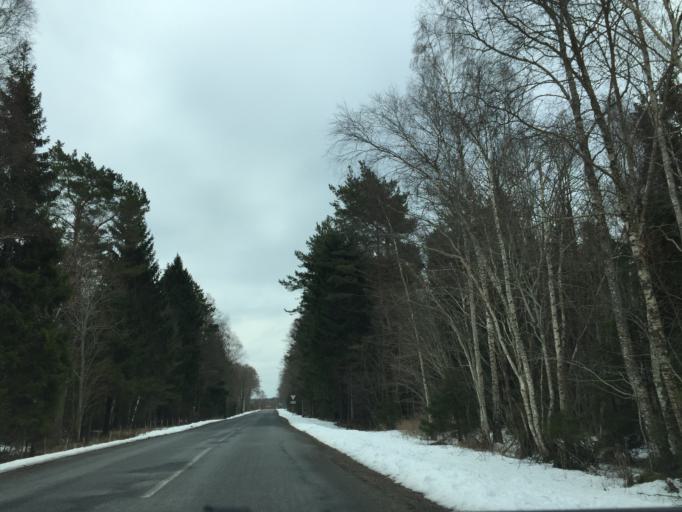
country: EE
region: Saare
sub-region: Kuressaare linn
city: Kuressaare
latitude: 58.4188
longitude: 22.1261
